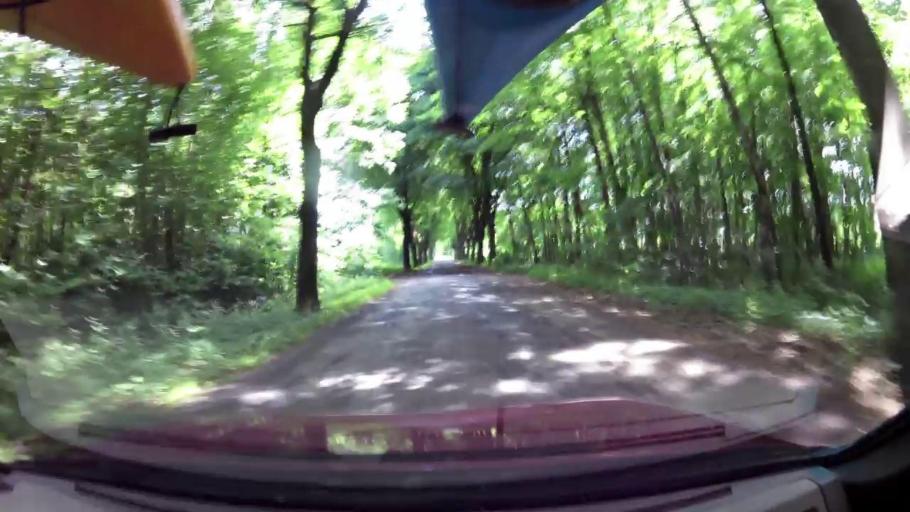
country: PL
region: West Pomeranian Voivodeship
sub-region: Powiat slawienski
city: Darlowo
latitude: 54.3260
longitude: 16.3660
